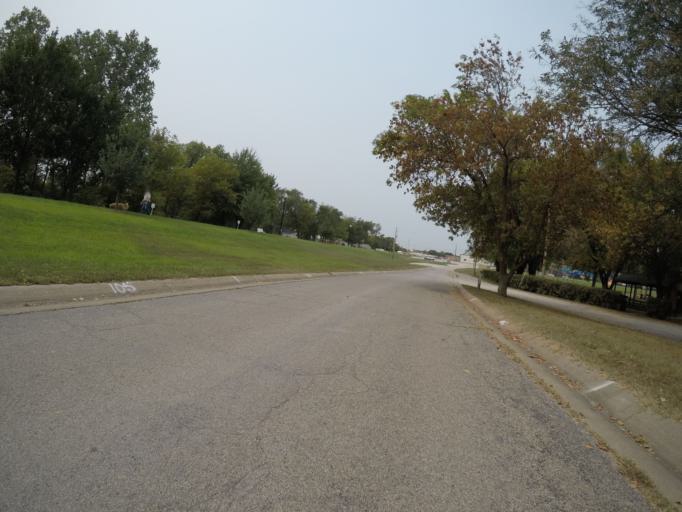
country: US
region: Kansas
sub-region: Marshall County
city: Marysville
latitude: 39.8383
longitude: -96.6473
